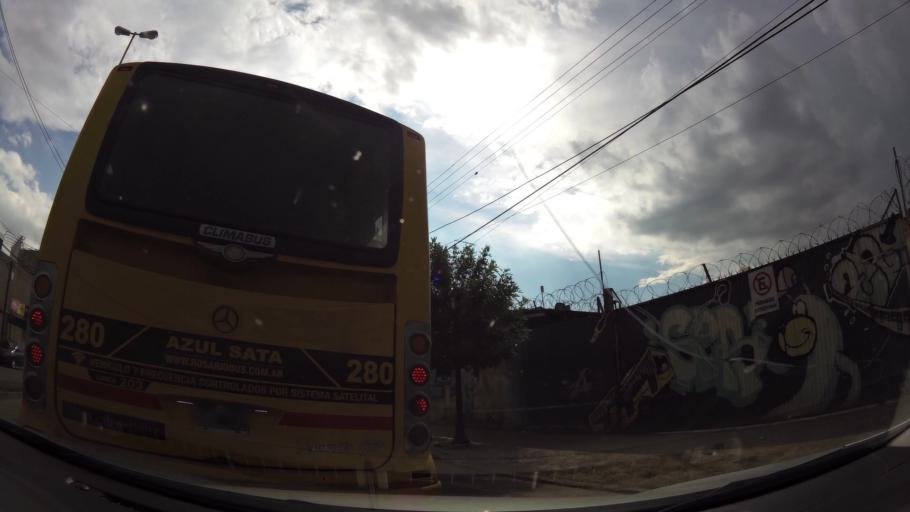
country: AR
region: Buenos Aires
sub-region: Partido de Tigre
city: Tigre
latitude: -34.4843
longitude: -58.6129
